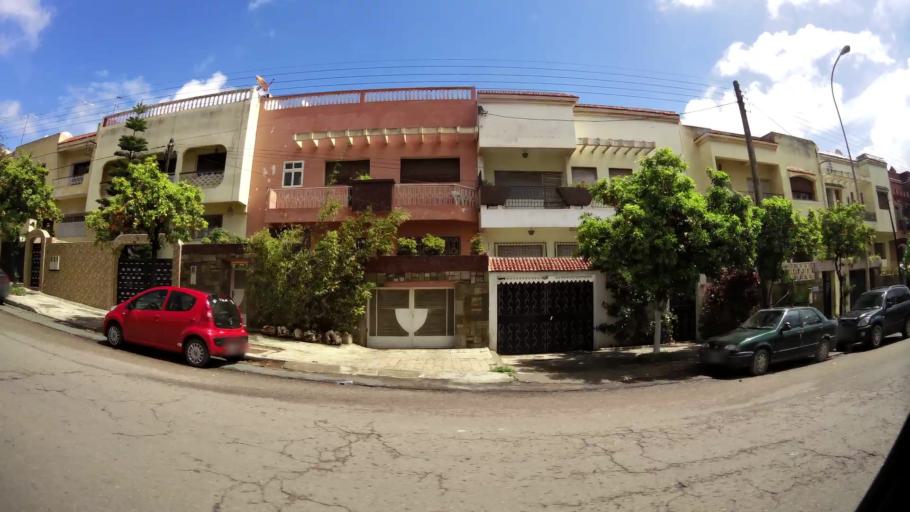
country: MA
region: Grand Casablanca
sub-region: Casablanca
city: Casablanca
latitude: 33.5568
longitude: -7.6769
